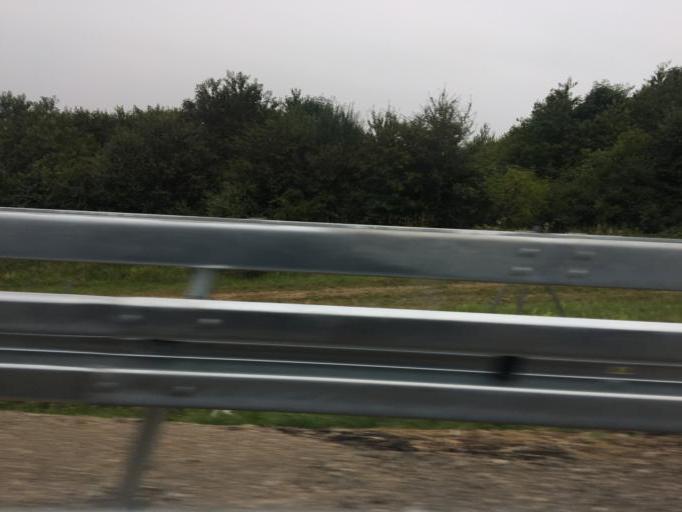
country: DE
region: Bavaria
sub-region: Upper Franconia
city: Pegnitz
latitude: 49.8186
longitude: 11.4972
